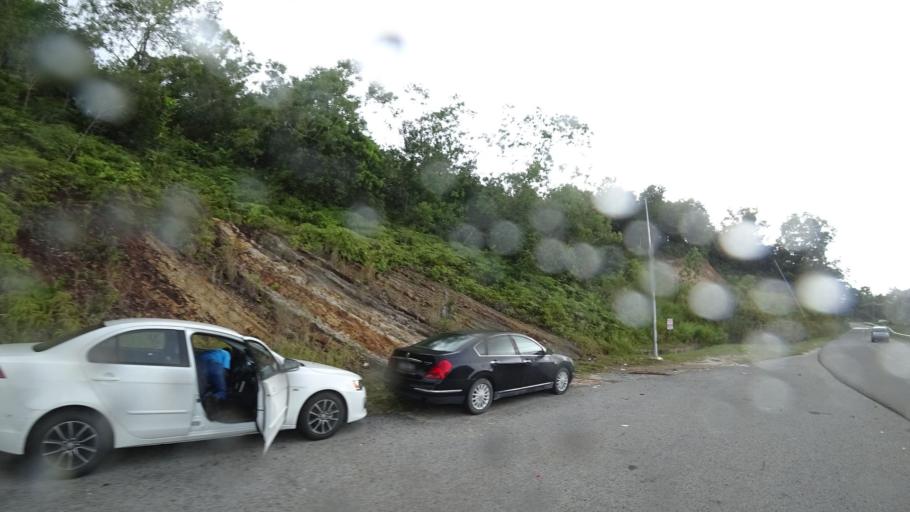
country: BN
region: Brunei and Muara
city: Bandar Seri Begawan
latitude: 4.8602
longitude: 114.9511
